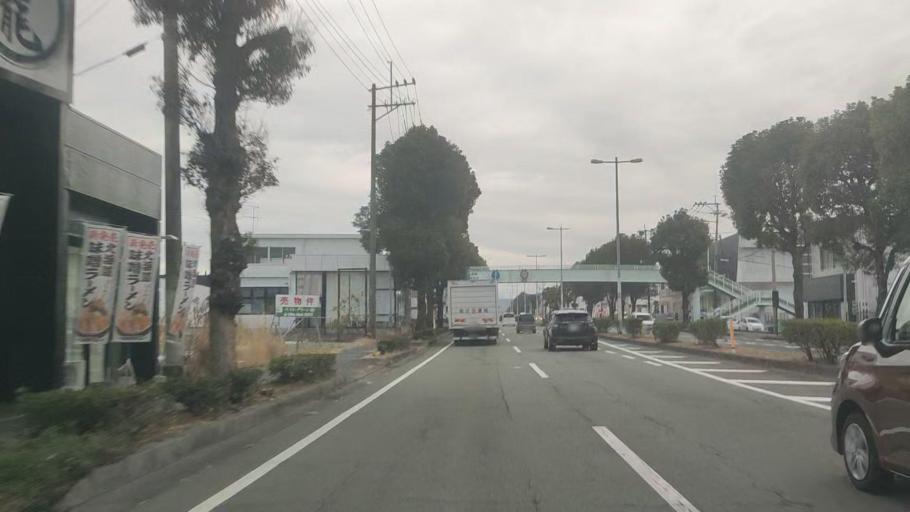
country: JP
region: Kumamoto
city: Kumamoto
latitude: 32.8234
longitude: 130.7617
